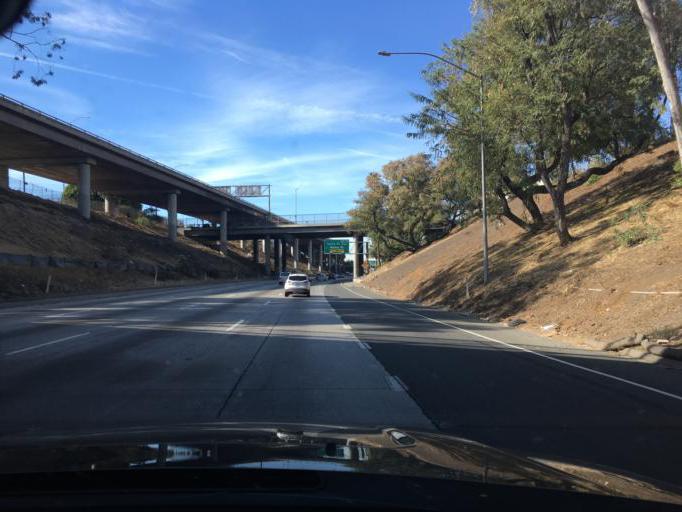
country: US
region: California
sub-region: Los Angeles County
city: Boyle Heights
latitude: 34.0296
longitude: -118.2188
